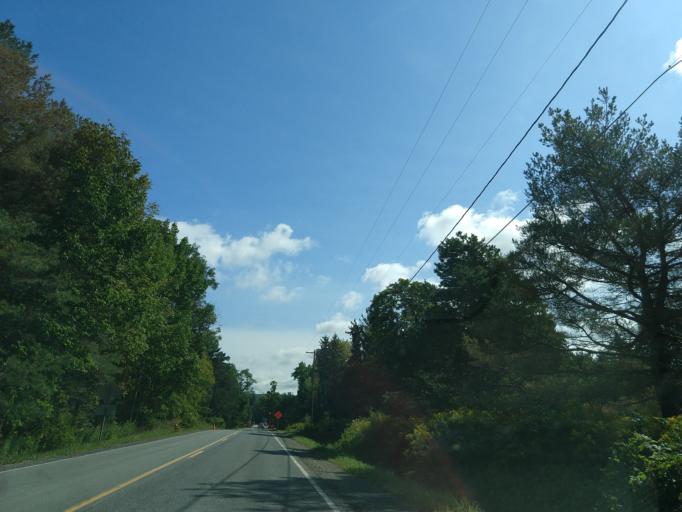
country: US
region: New York
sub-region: Tompkins County
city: East Ithaca
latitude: 42.4060
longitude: -76.4669
